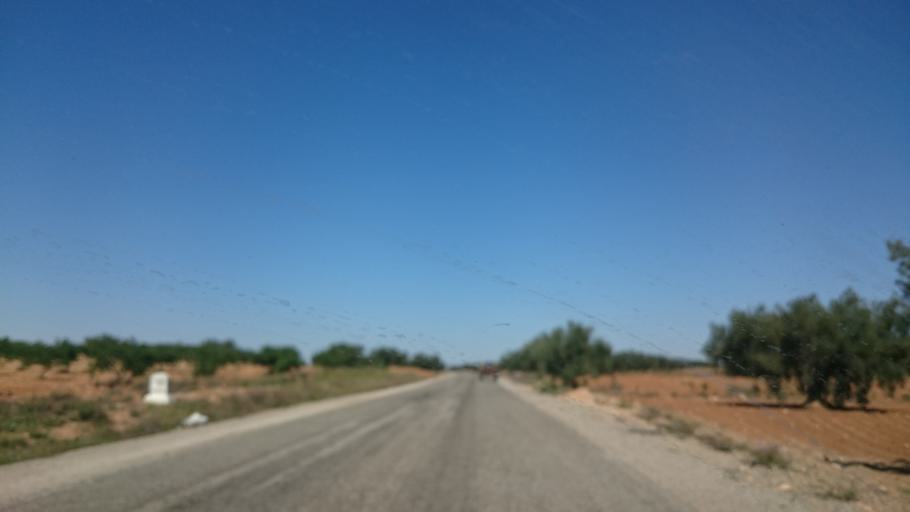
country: TN
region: Safaqis
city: Bi'r `Ali Bin Khalifah
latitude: 34.8628
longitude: 10.4148
